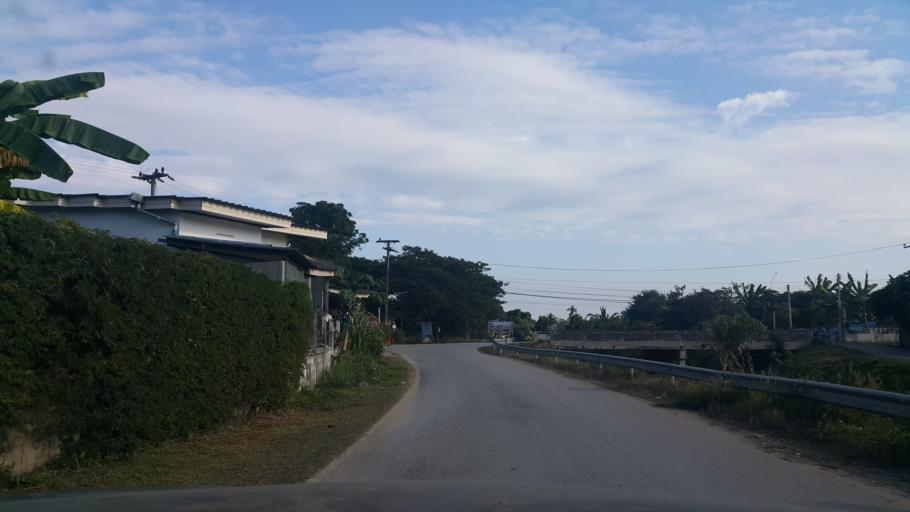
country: TH
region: Lampang
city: Hang Chat
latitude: 18.3145
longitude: 99.3502
